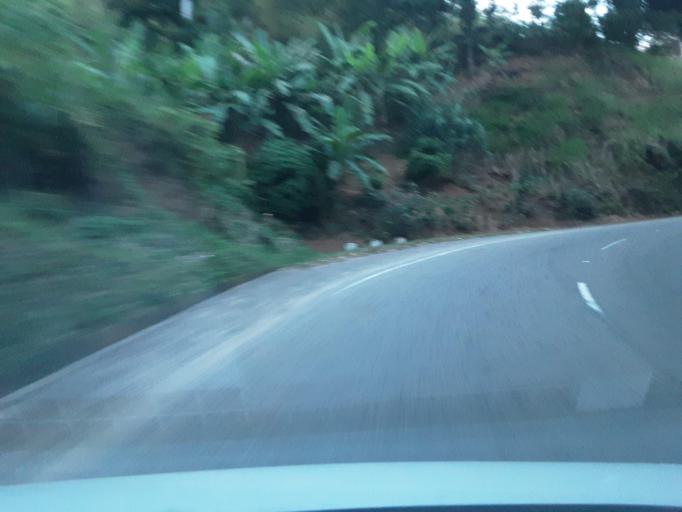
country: LK
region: Uva
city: Badulla
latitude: 6.9137
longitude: 80.9544
